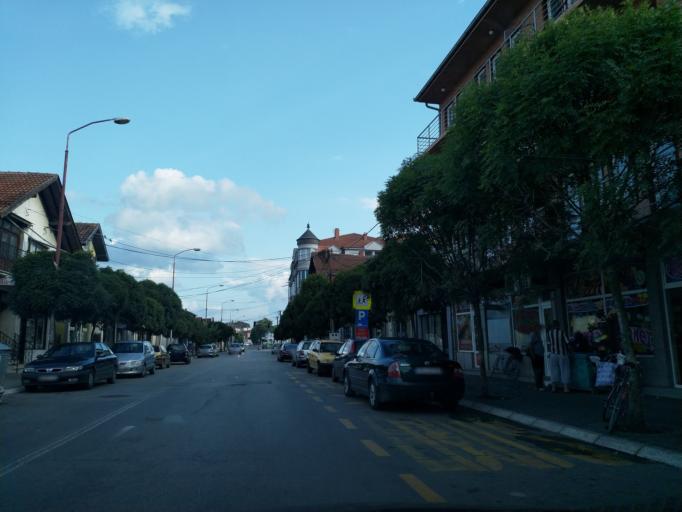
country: RS
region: Central Serbia
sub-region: Pomoravski Okrug
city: Paracin
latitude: 43.8566
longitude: 21.4120
